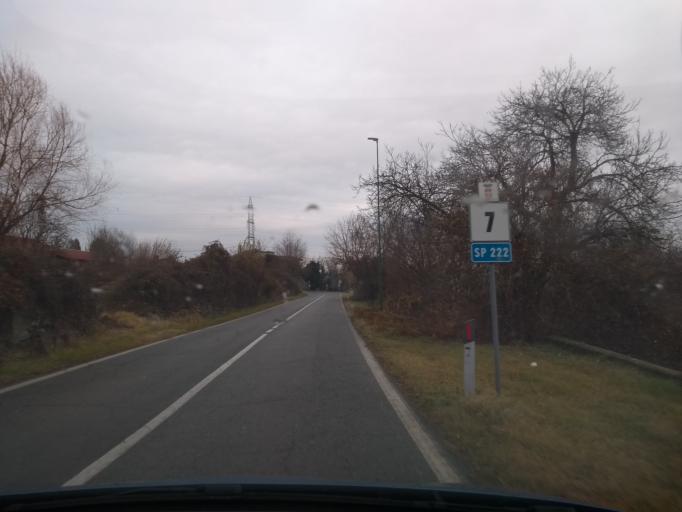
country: IT
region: Piedmont
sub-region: Provincia di Torino
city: Strambinello
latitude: 45.4234
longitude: 7.7753
